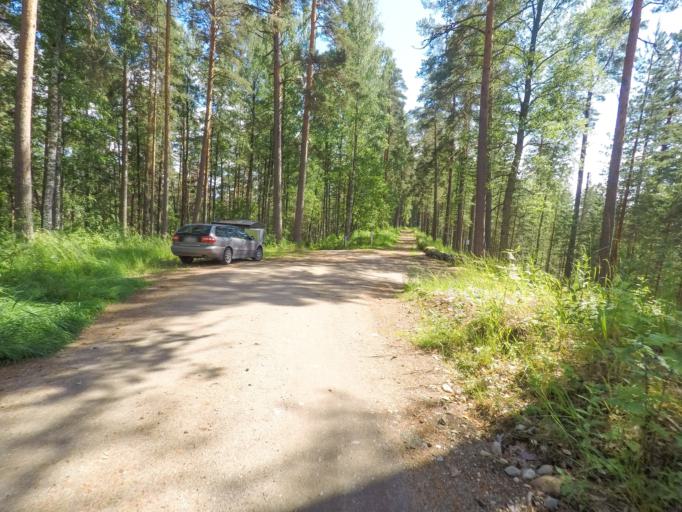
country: FI
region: Southern Savonia
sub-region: Savonlinna
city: Punkaharju
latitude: 61.8004
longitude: 29.3082
